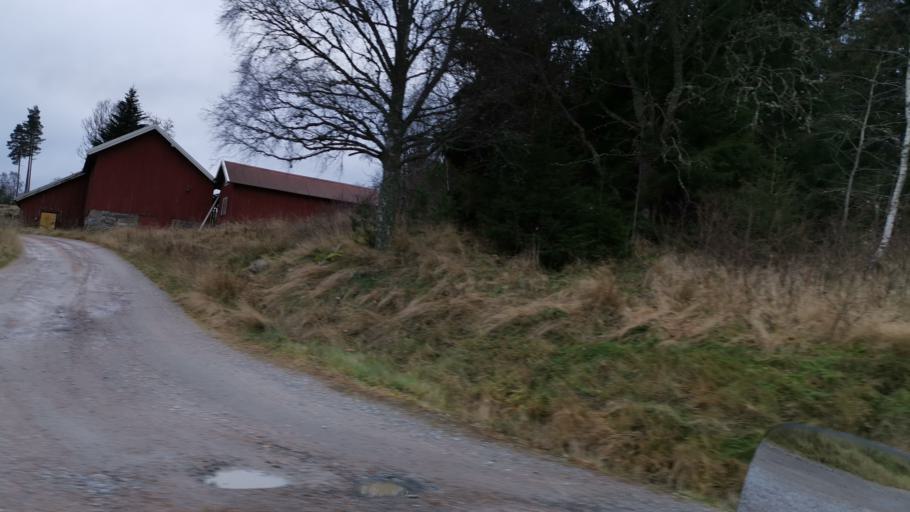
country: SE
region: Vaestra Goetaland
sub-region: Orust
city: Henan
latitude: 58.2176
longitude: 11.7136
